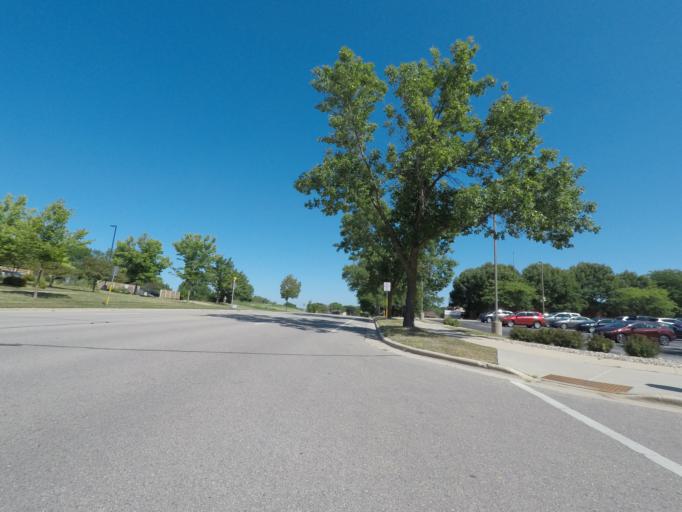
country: US
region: Wisconsin
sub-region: Dane County
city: Verona
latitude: 43.0336
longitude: -89.4968
